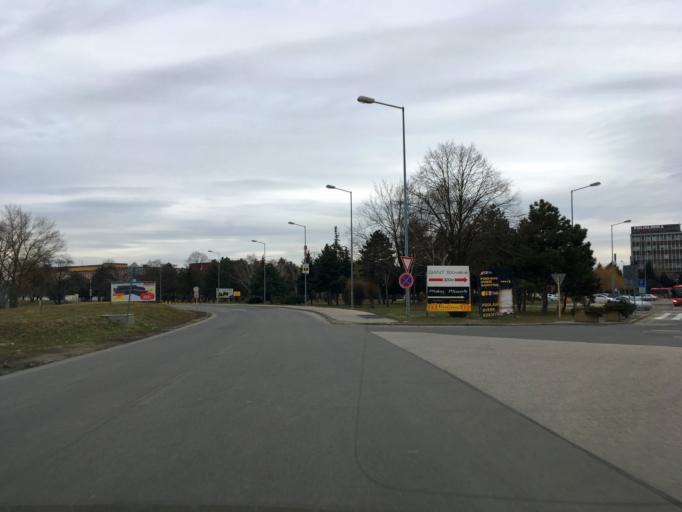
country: SK
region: Bratislavsky
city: Bratislava
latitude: 48.1303
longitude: 17.1740
